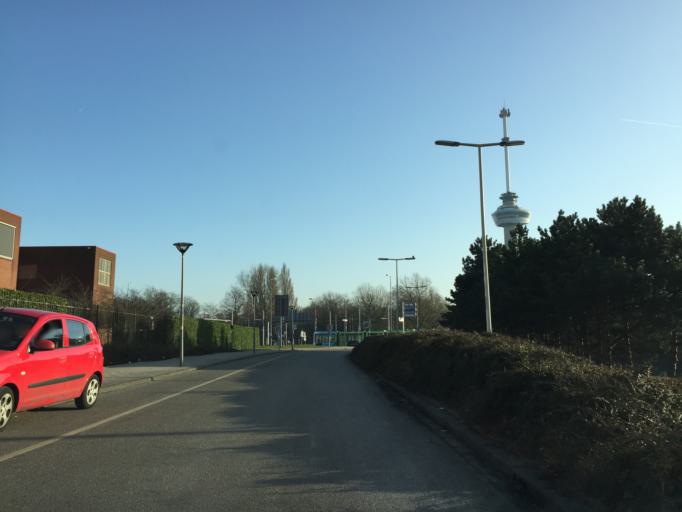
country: NL
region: South Holland
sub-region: Gemeente Rotterdam
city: Delfshaven
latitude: 51.9094
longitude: 4.4658
